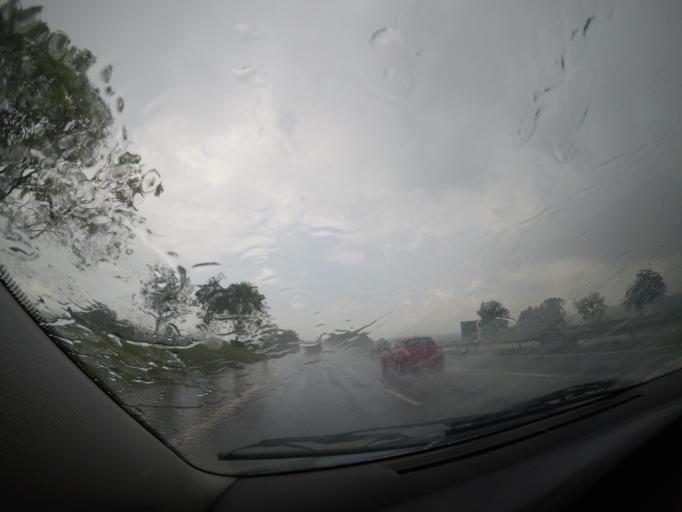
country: GB
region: England
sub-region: Cumbria
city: Penrith
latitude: 54.7118
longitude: -2.7950
